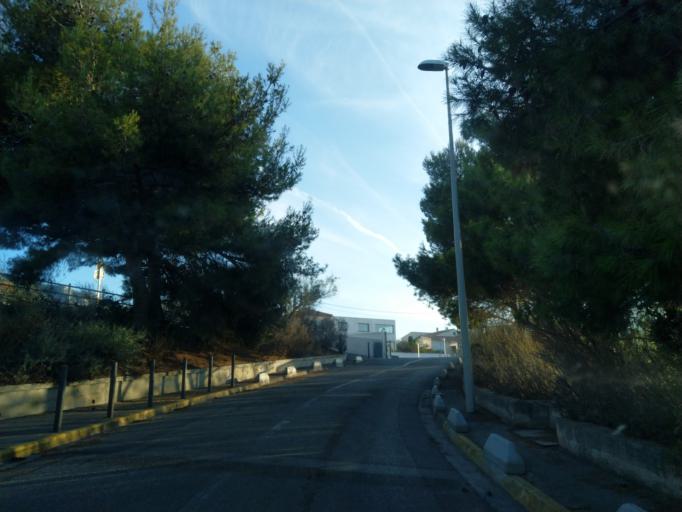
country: FR
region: Provence-Alpes-Cote d'Azur
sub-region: Departement des Bouches-du-Rhone
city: Marseille 08
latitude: 43.2426
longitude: 5.3675
